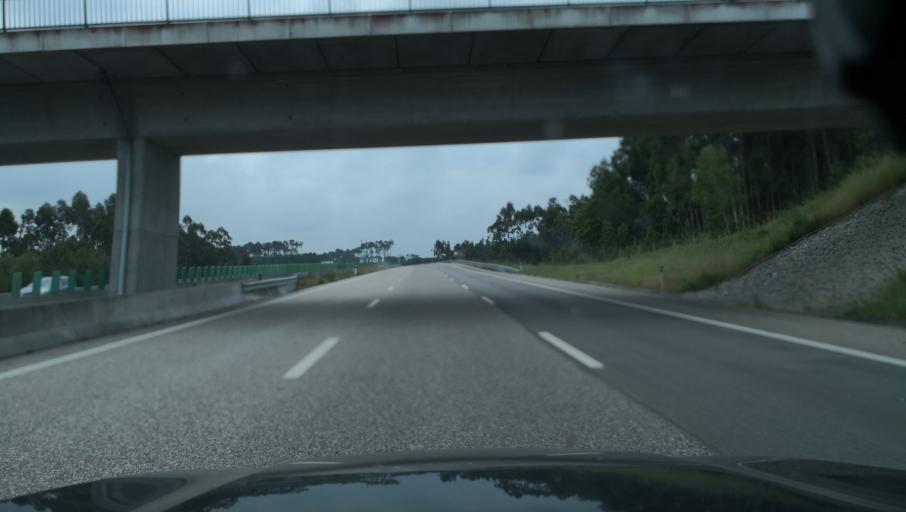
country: PT
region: Coimbra
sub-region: Figueira da Foz
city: Lavos
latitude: 40.0275
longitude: -8.8136
